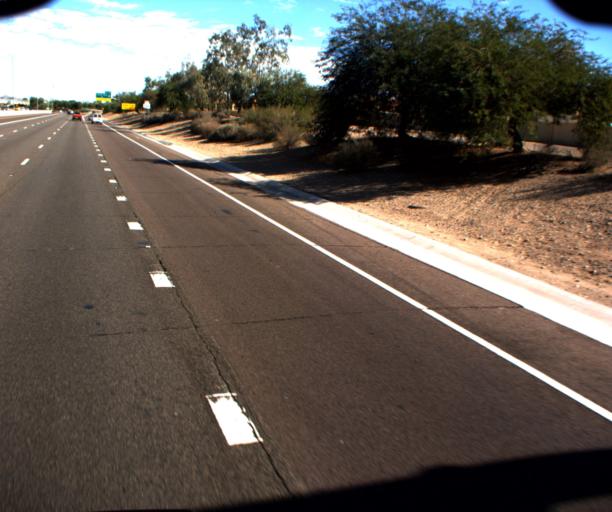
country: US
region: Arizona
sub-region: Maricopa County
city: Sun City
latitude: 33.6453
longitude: -112.2344
